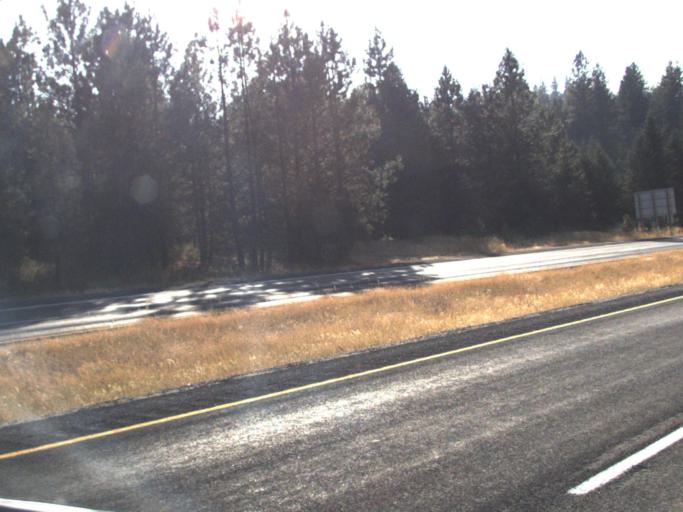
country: US
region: Washington
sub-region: Spokane County
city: Deer Park
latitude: 48.0970
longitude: -117.2908
